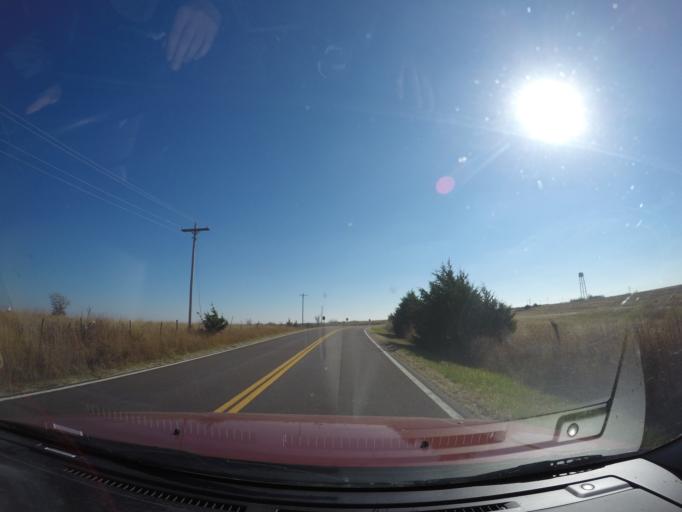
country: US
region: Kansas
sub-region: Geary County
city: Grandview Plaza
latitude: 39.0232
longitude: -96.7631
